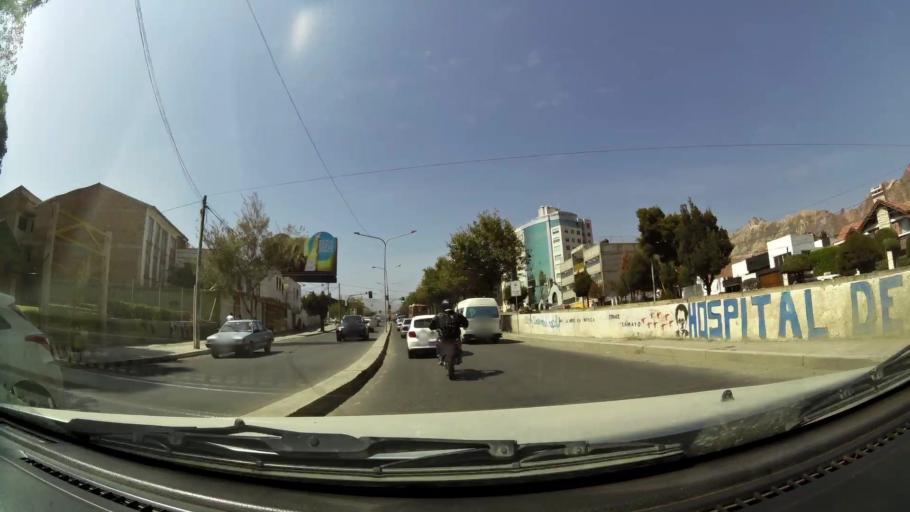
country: BO
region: La Paz
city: La Paz
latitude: -16.5456
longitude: -68.0922
